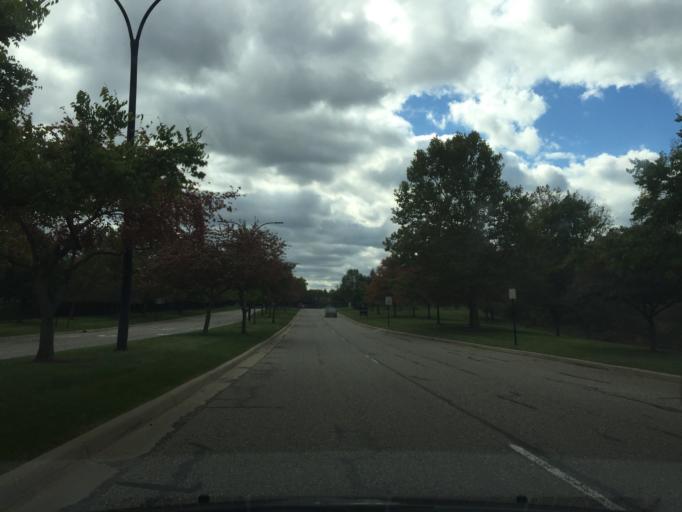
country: US
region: Michigan
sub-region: Oakland County
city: Auburn Hills
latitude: 42.6562
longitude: -83.2360
